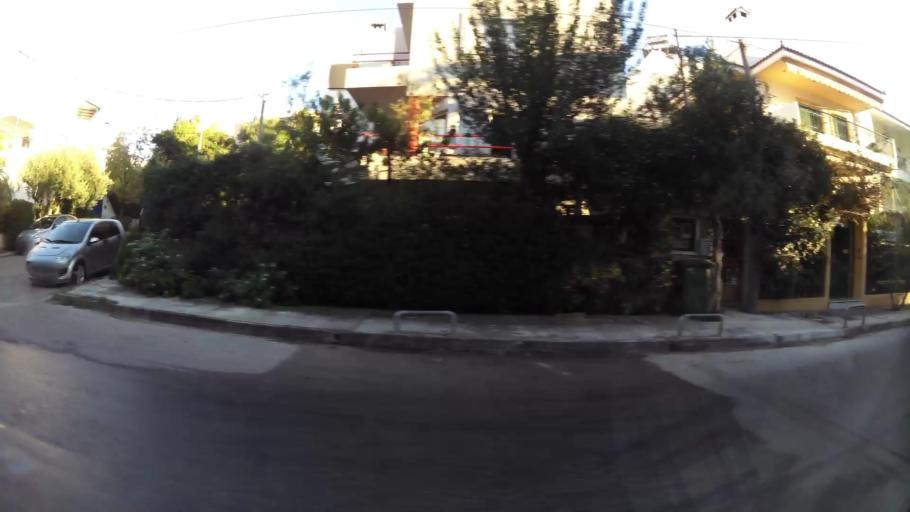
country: GR
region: Attica
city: Pefki
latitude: 38.0689
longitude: 23.7983
